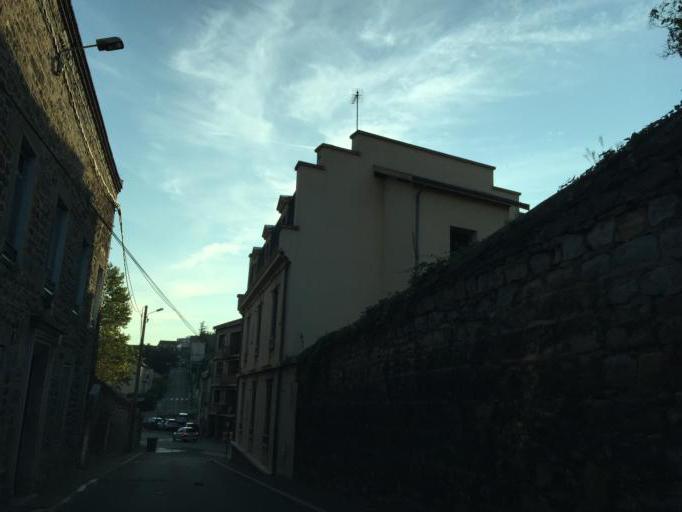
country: FR
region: Rhone-Alpes
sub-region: Departement de la Loire
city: Saint-Chamond
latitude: 45.4807
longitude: 4.5145
